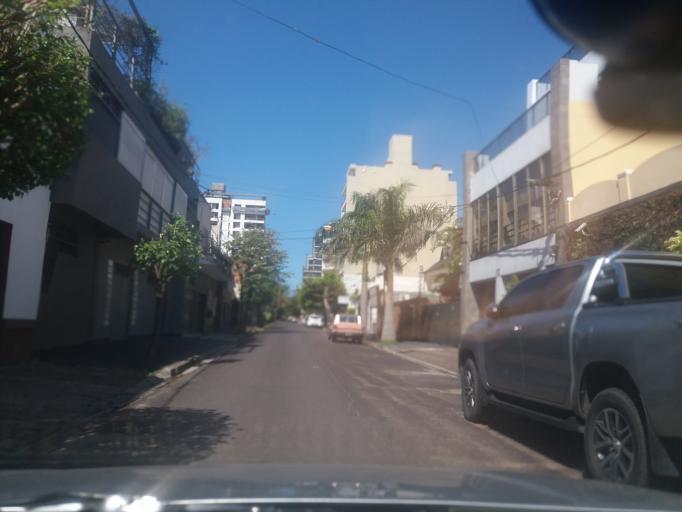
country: AR
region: Corrientes
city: Corrientes
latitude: -27.4658
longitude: -58.8467
